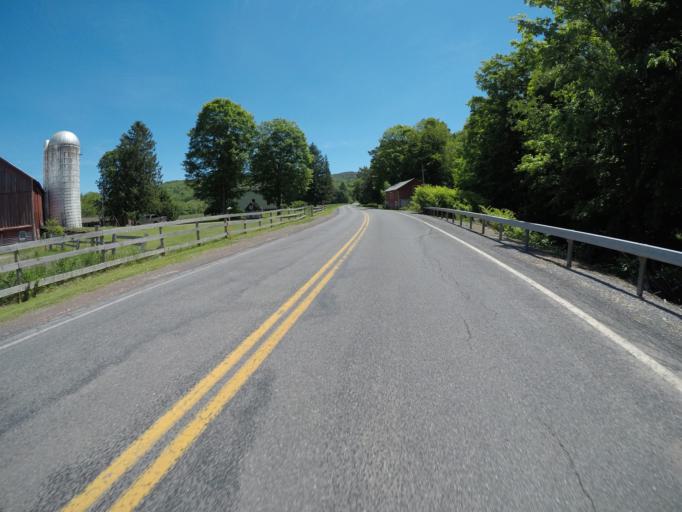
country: US
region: New York
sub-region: Delaware County
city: Delhi
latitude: 42.2169
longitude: -74.8881
